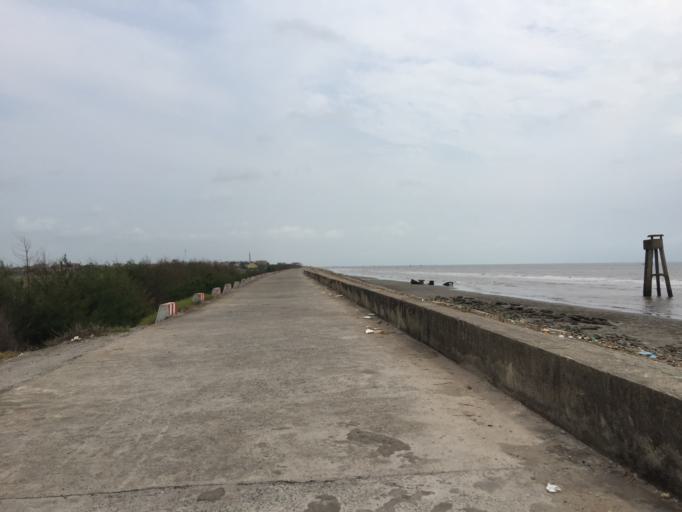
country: VN
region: Ninh Binh
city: Thi Tran Phat Diem
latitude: 20.0137
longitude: 106.2088
